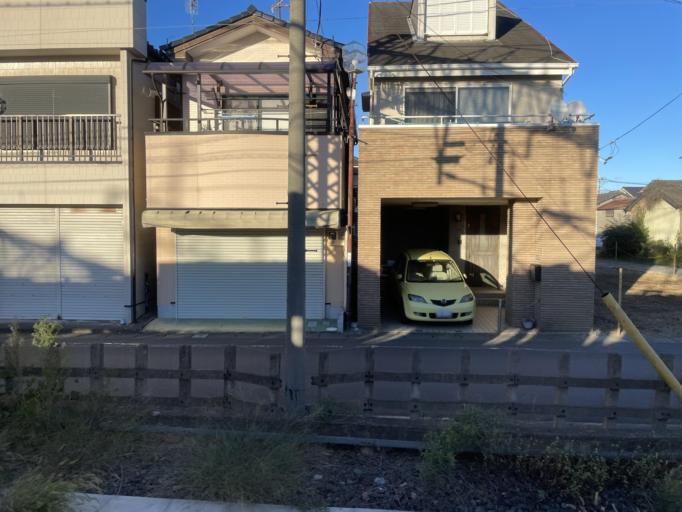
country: JP
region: Saitama
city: Sugito
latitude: 36.0240
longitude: 139.7287
